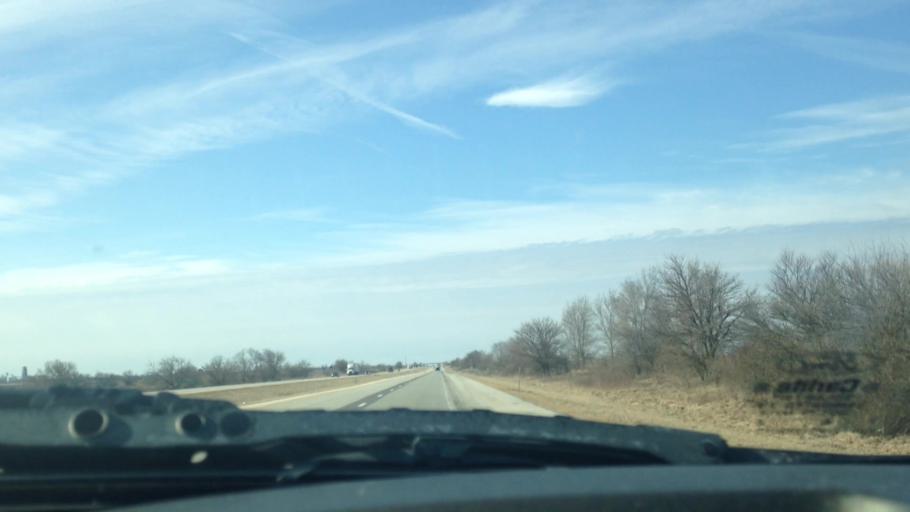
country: US
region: Illinois
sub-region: Ford County
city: Paxton
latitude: 40.5062
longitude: -88.0856
